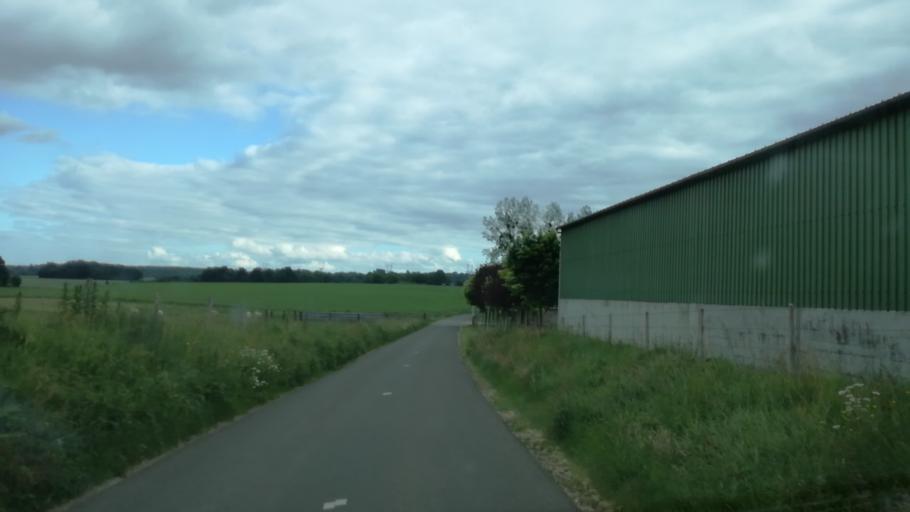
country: FR
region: Haute-Normandie
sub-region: Departement de l'Eure
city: Bourg-Achard
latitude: 49.2842
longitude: 0.8112
